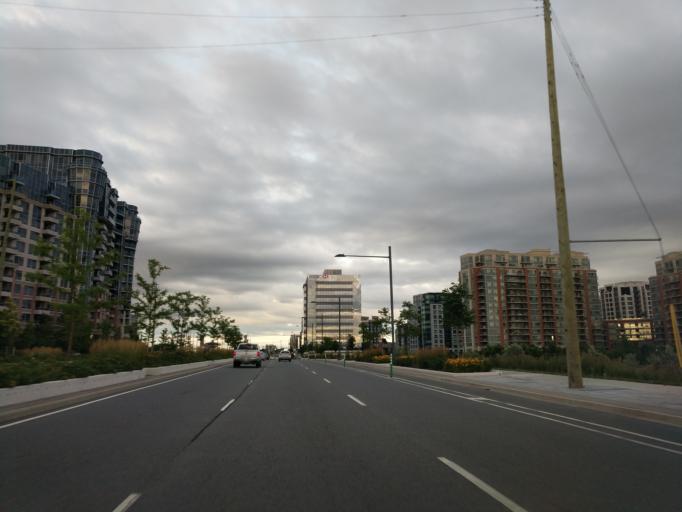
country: CA
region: Ontario
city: Markham
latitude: 43.8533
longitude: -79.3420
